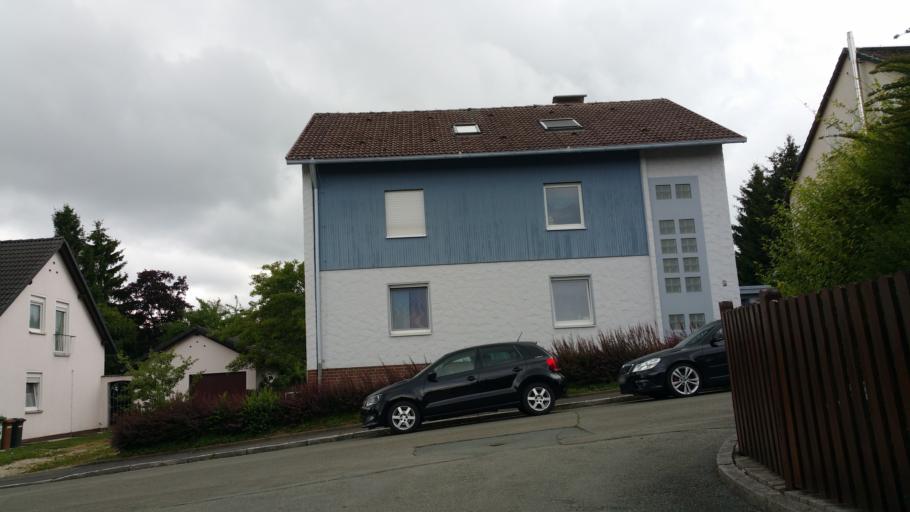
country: DE
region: Bavaria
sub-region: Upper Franconia
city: Rehau
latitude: 50.2546
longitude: 12.0368
